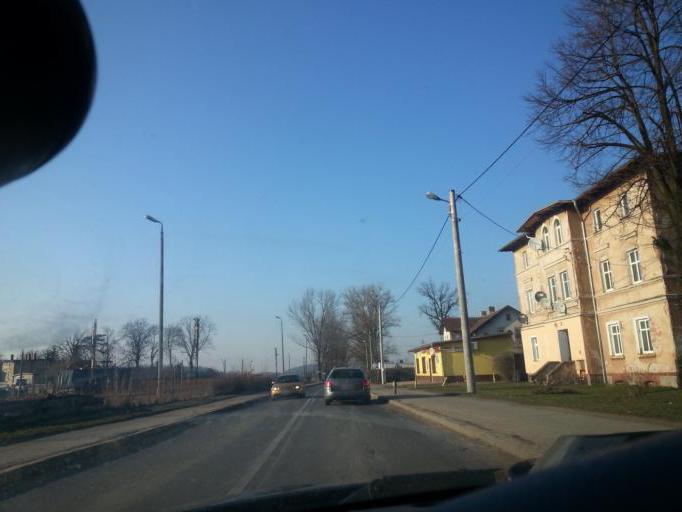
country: PL
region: Lower Silesian Voivodeship
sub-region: Powiat jeleniogorski
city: Myslakowice
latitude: 50.8357
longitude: 15.7884
